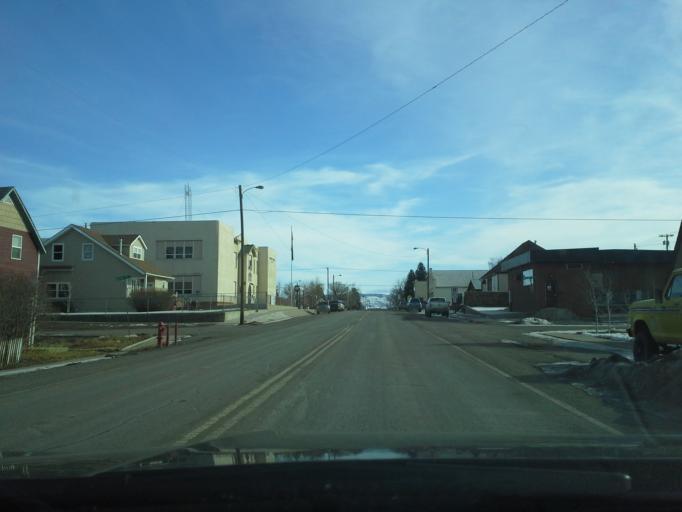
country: US
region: Montana
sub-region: Lewis and Clark County
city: East Helena
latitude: 46.5895
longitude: -111.9166
